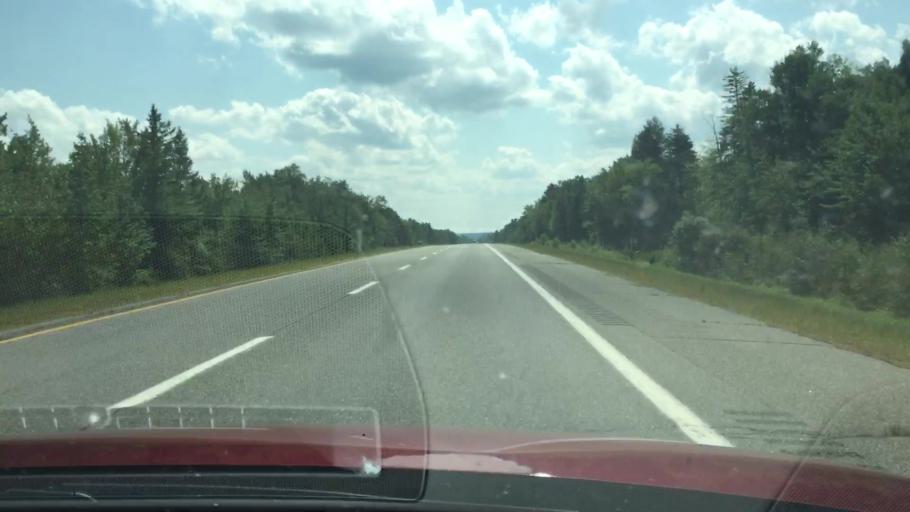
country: US
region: Maine
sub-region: Penobscot County
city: Lincoln
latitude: 45.4197
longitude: -68.5917
